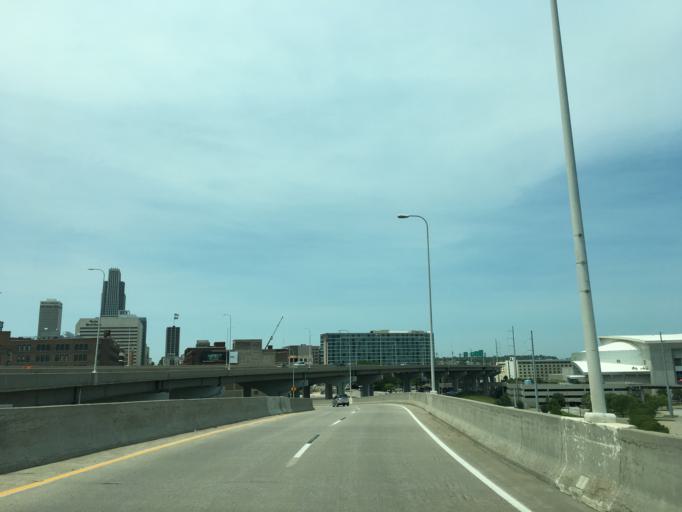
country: US
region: Nebraska
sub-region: Douglas County
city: Omaha
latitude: 41.2596
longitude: -95.9243
